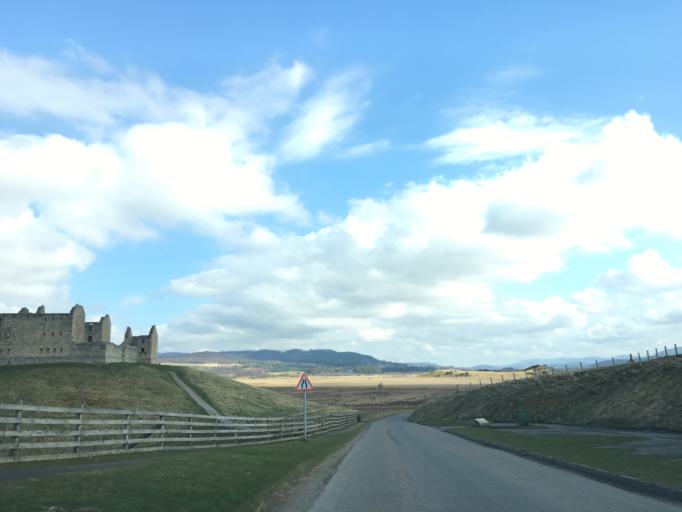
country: GB
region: Scotland
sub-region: Highland
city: Kingussie
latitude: 57.0709
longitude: -4.0397
